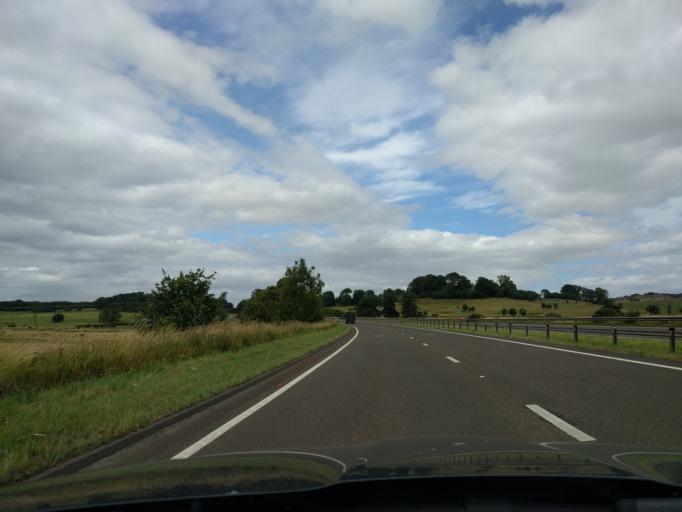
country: GB
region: England
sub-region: Northumberland
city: Alnwick
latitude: 55.4150
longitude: -1.6768
